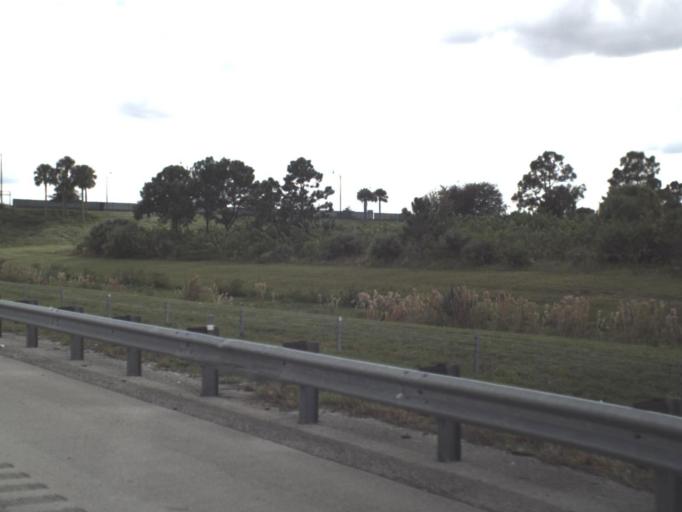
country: US
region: Florida
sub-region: Saint Lucie County
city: Port Saint Lucie
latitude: 27.2969
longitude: -80.3717
